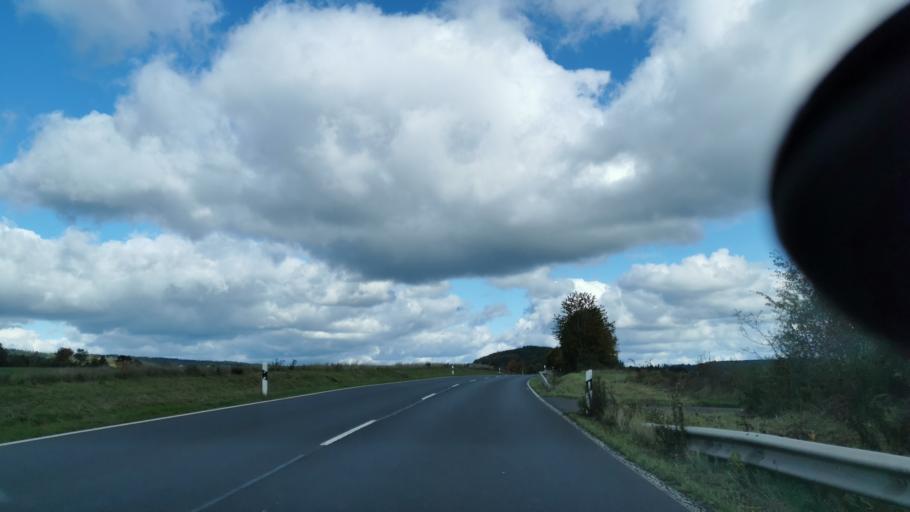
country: DE
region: Rheinland-Pfalz
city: Walsdorf
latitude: 50.3024
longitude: 6.7227
